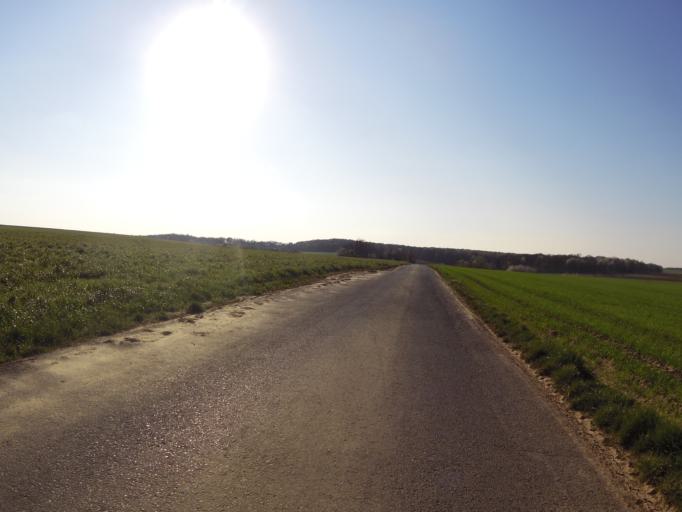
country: DE
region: Bavaria
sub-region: Regierungsbezirk Unterfranken
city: Oberpleichfeld
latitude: 49.8258
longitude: 10.0848
